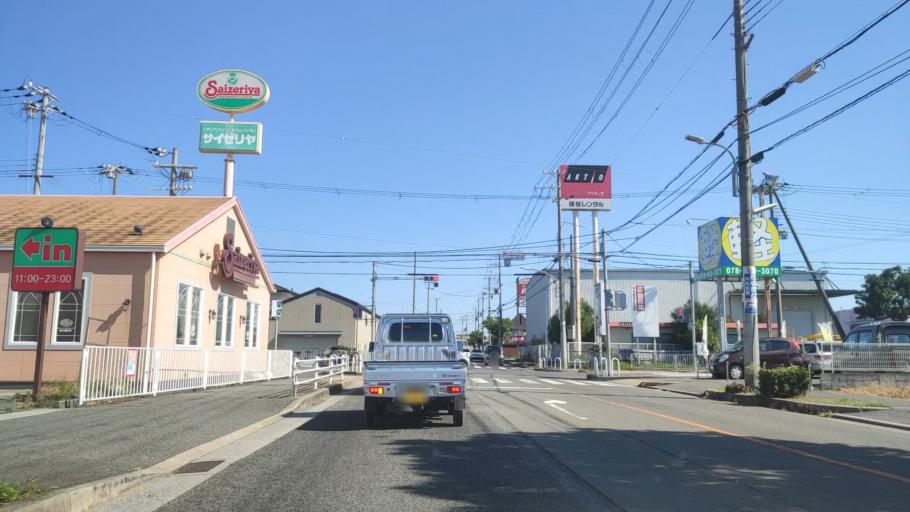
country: JP
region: Hyogo
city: Akashi
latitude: 34.6610
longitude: 134.9908
